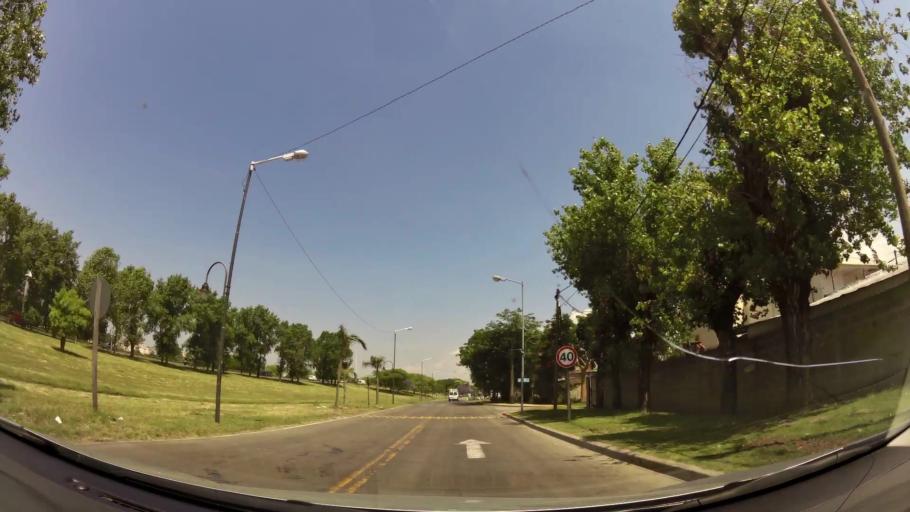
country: AR
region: Buenos Aires
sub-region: Partido de Tigre
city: Tigre
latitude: -34.4510
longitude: -58.5764
